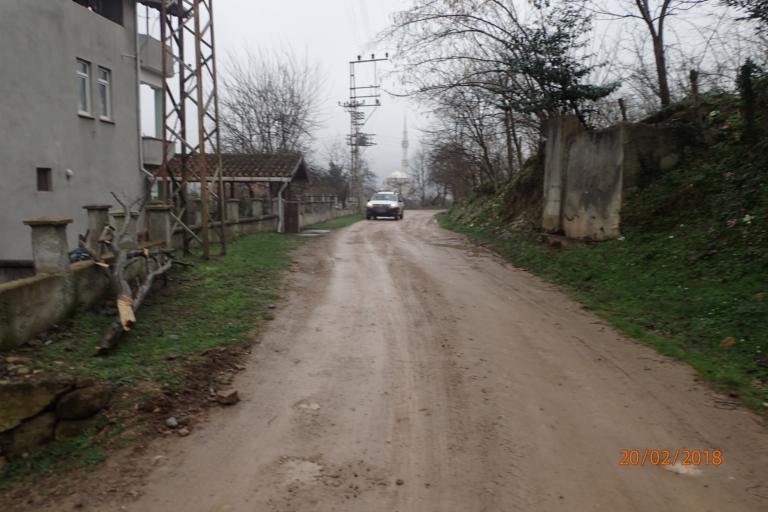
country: TR
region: Ordu
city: Camas
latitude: 40.9481
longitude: 37.5206
